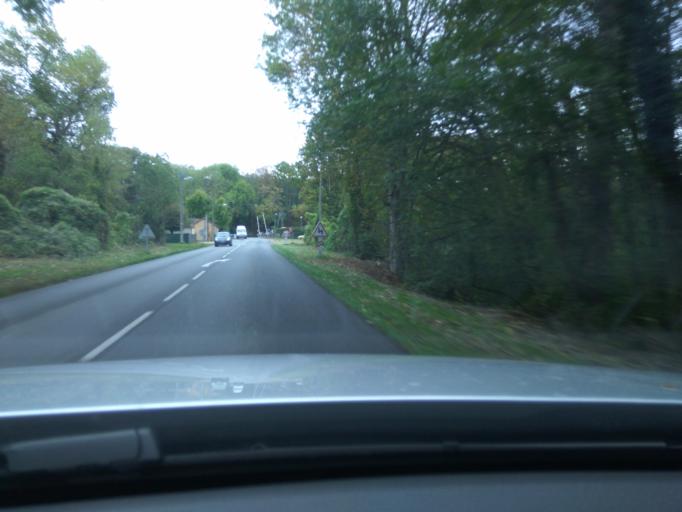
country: FR
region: Centre
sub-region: Departement du Cher
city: Saint-Satur
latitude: 47.3382
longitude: 2.8786
